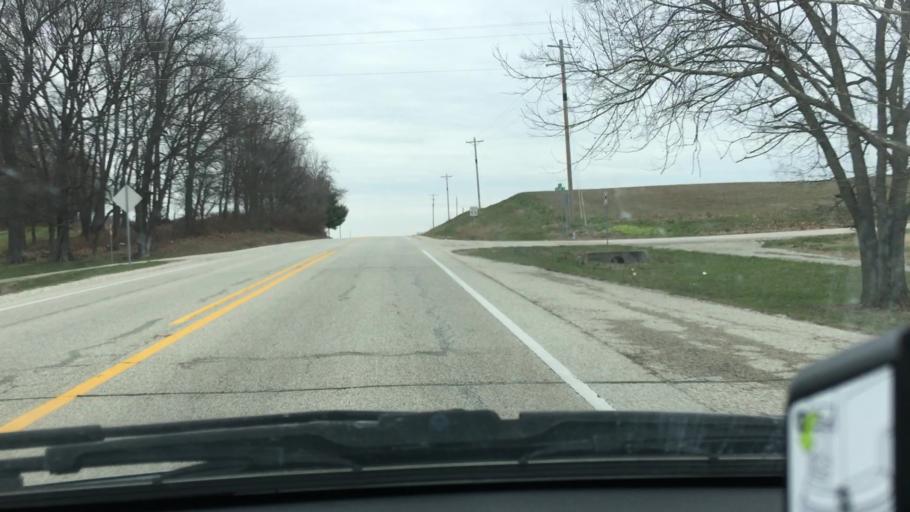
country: US
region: Indiana
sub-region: Greene County
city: Bloomfield
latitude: 38.9941
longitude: -87.0163
